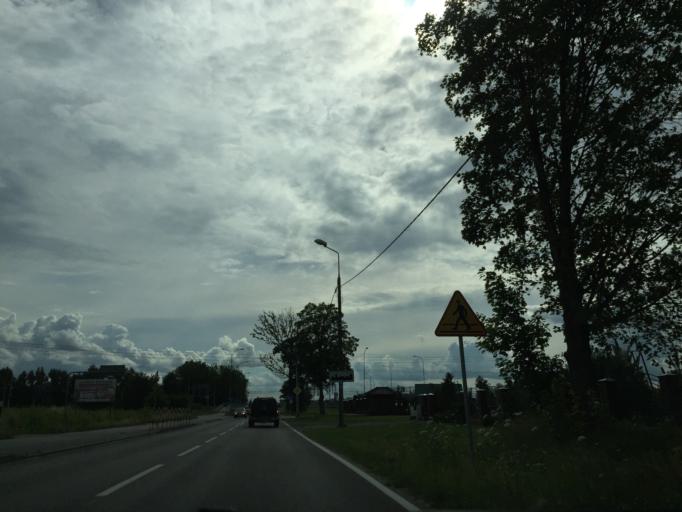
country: PL
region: Lublin Voivodeship
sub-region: Powiat lukowski
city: Lukow
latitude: 51.9392
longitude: 22.4030
